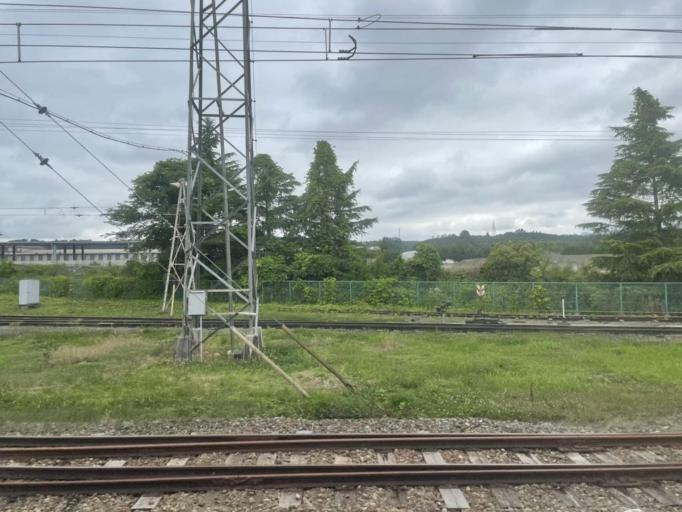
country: JP
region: Saitama
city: Chichibu
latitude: 36.0316
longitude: 139.0972
